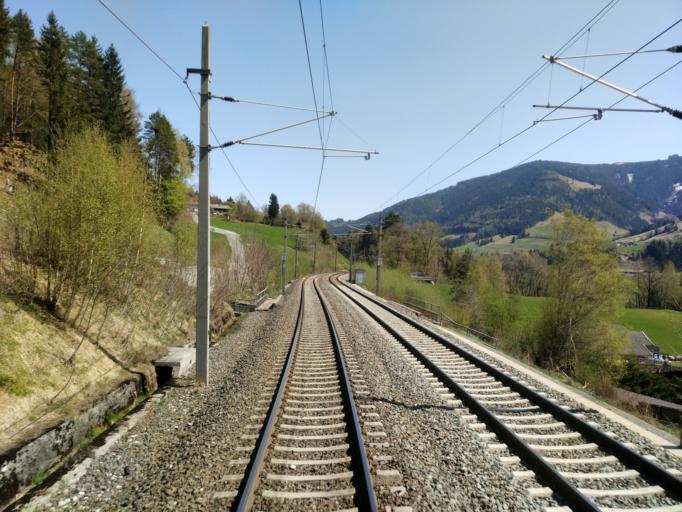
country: AT
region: Salzburg
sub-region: Politischer Bezirk Zell am See
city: Leogang
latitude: 47.4420
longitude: 12.7455
